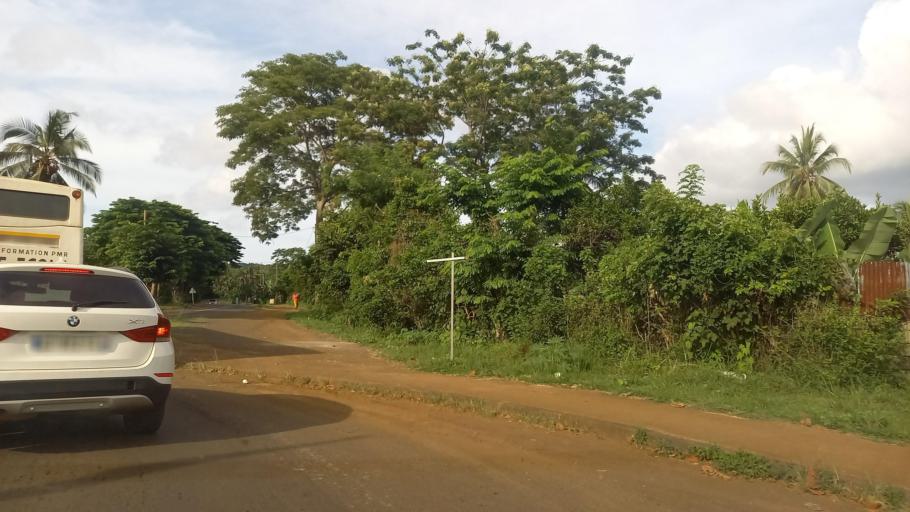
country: YT
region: Tsingoni
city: Tsingoni
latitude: -12.7914
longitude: 45.1254
